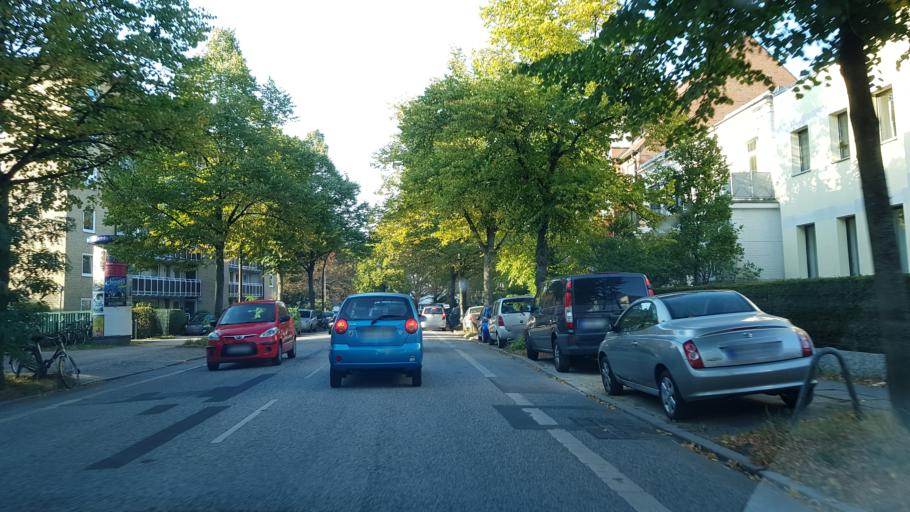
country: DE
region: Hamburg
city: Barmbek-Nord
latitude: 53.5902
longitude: 10.0499
